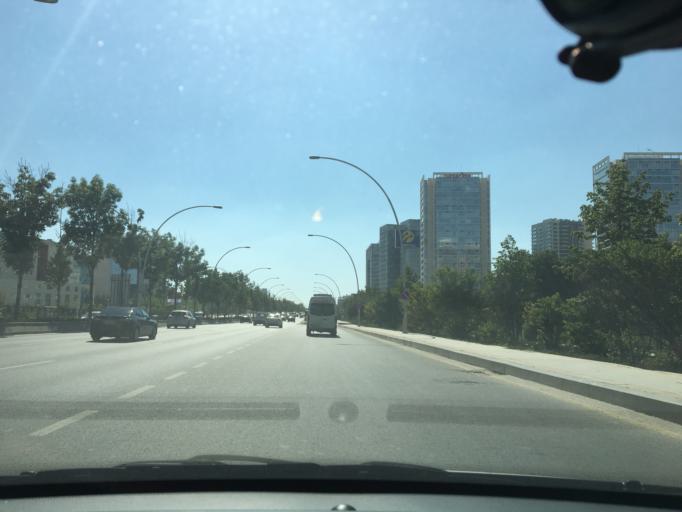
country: TR
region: Ankara
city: Batikent
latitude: 39.9077
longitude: 32.7591
